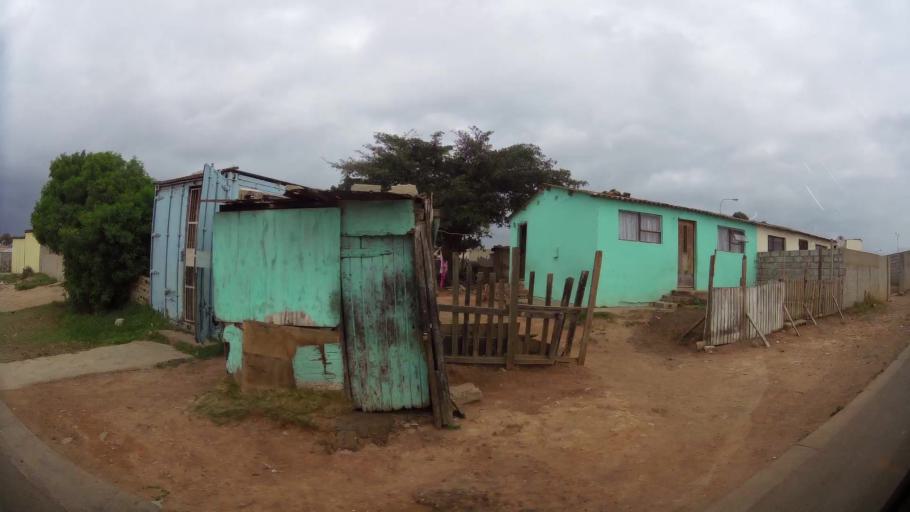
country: ZA
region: Eastern Cape
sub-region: Nelson Mandela Bay Metropolitan Municipality
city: Port Elizabeth
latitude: -33.8756
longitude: 25.5628
